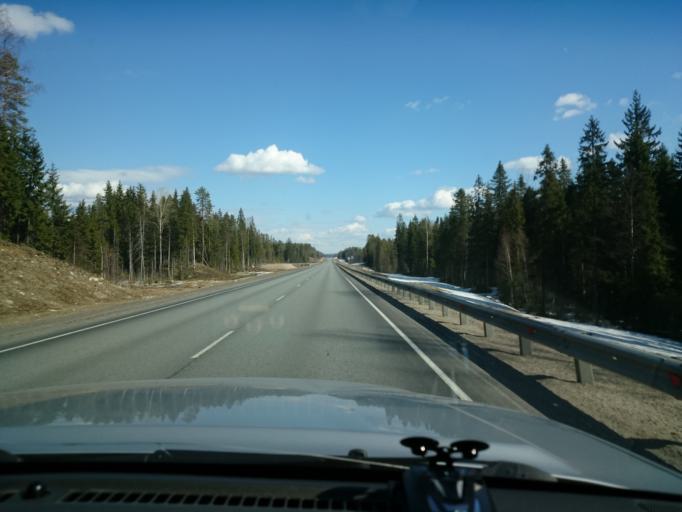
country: RU
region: Republic of Karelia
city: Pryazha
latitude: 61.5186
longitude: 33.4620
